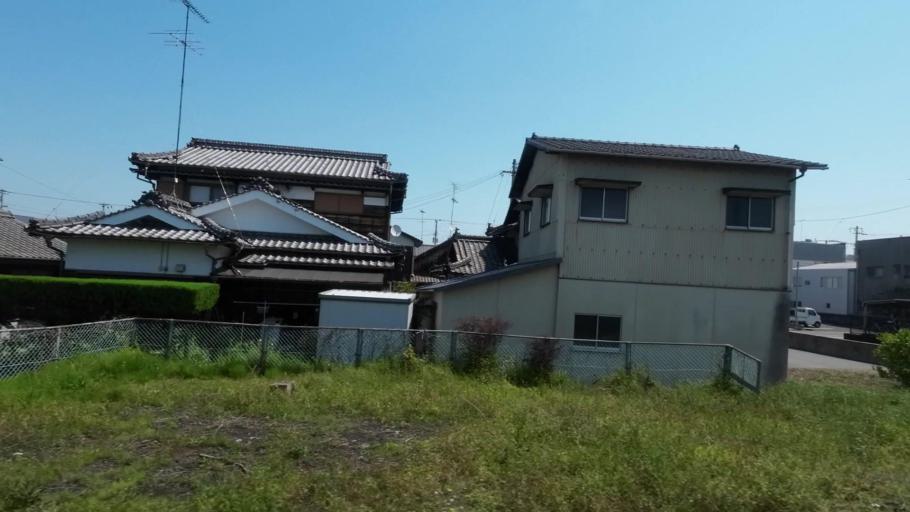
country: JP
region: Ehime
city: Saijo
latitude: 33.9305
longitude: 133.0849
